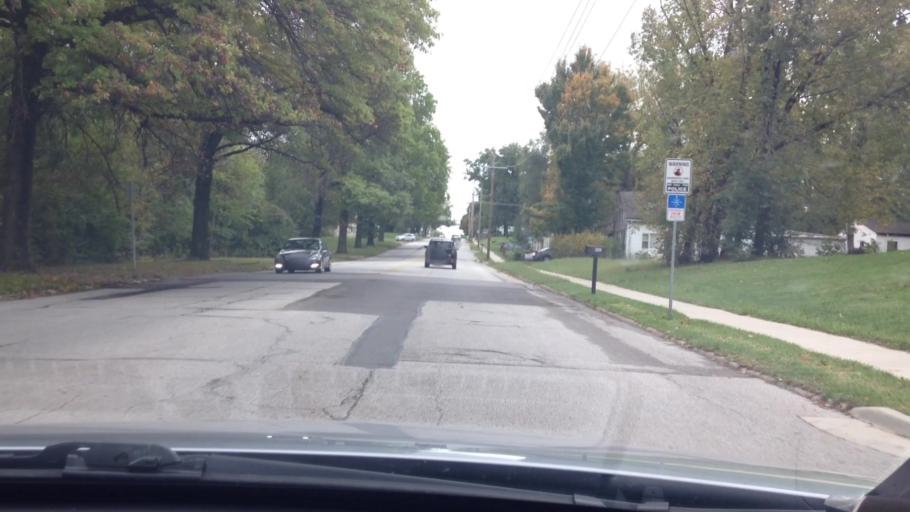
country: US
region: Kansas
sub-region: Leavenworth County
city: Leavenworth
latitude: 39.3049
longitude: -94.9275
